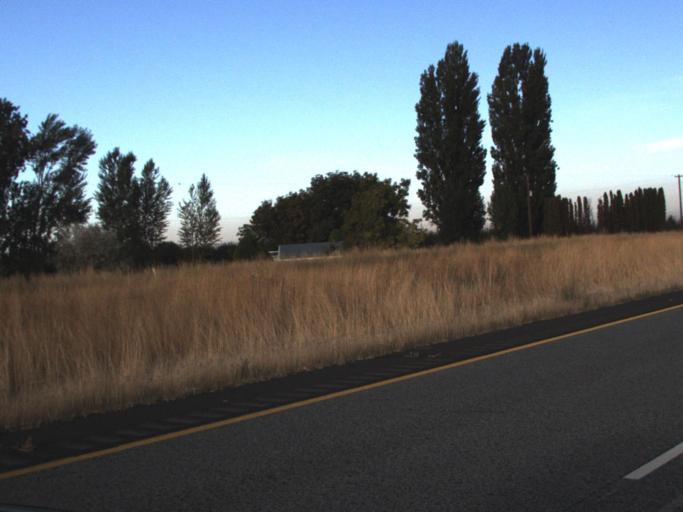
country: US
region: Washington
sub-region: Yakima County
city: Grandview
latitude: 46.2617
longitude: -119.8897
